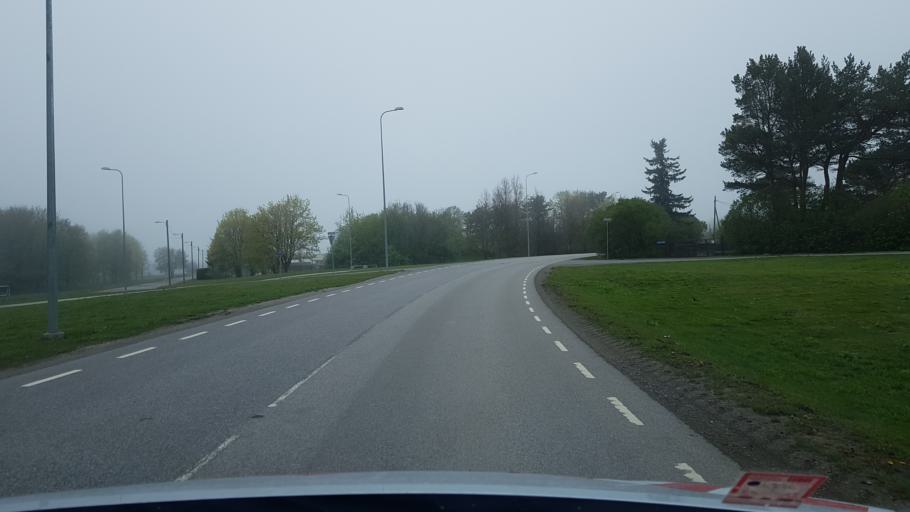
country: EE
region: Harju
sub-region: Joelaehtme vald
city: Loo
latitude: 59.4328
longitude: 24.9389
